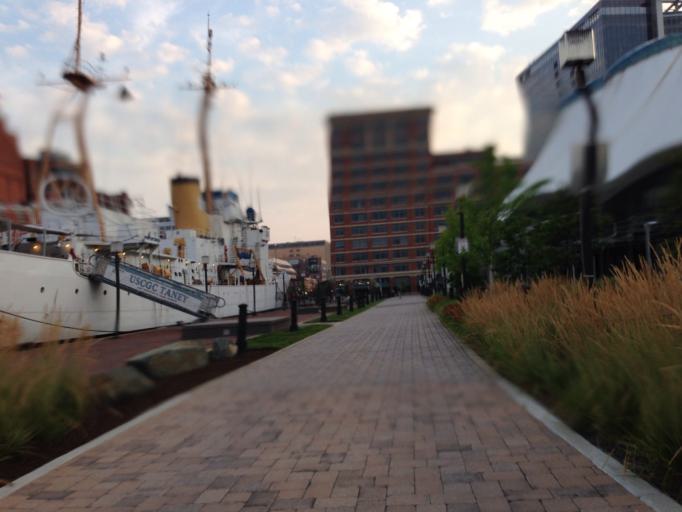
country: US
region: Maryland
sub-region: City of Baltimore
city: Baltimore
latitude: 39.2852
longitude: -76.6059
